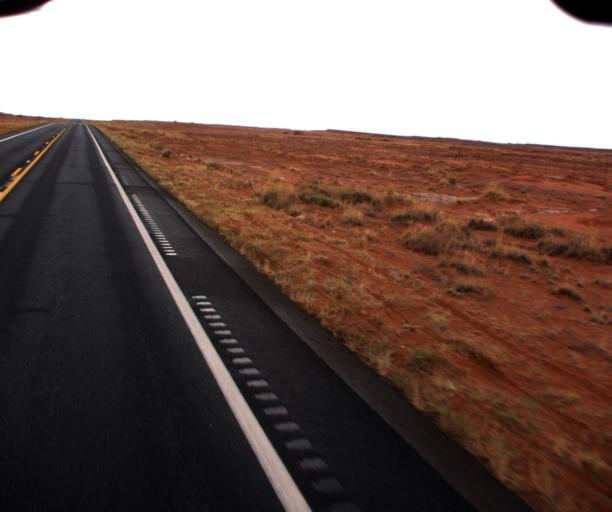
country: US
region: Arizona
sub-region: Coconino County
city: Tuba City
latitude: 36.1016
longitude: -111.3012
